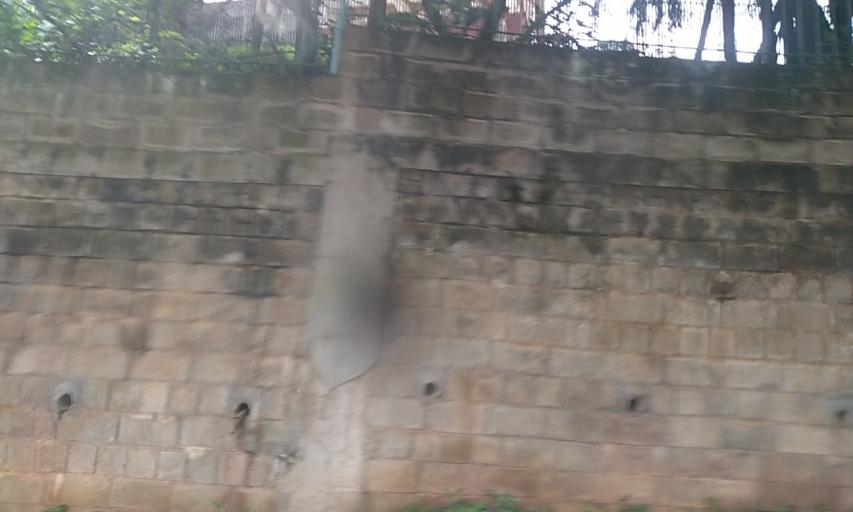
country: UG
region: Central Region
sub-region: Kampala District
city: Kampala
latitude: 0.3343
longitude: 32.5940
